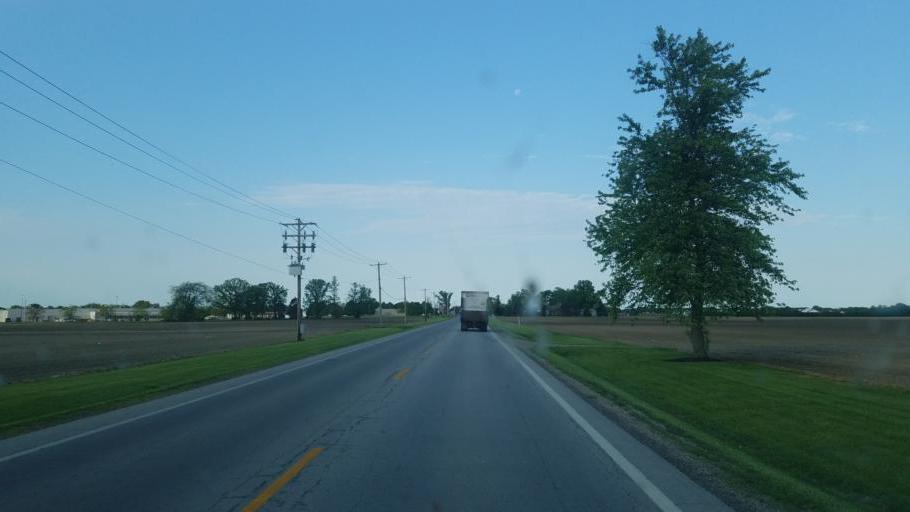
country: US
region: Ohio
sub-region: Fayette County
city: Washington Court House
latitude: 39.5575
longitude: -83.4158
